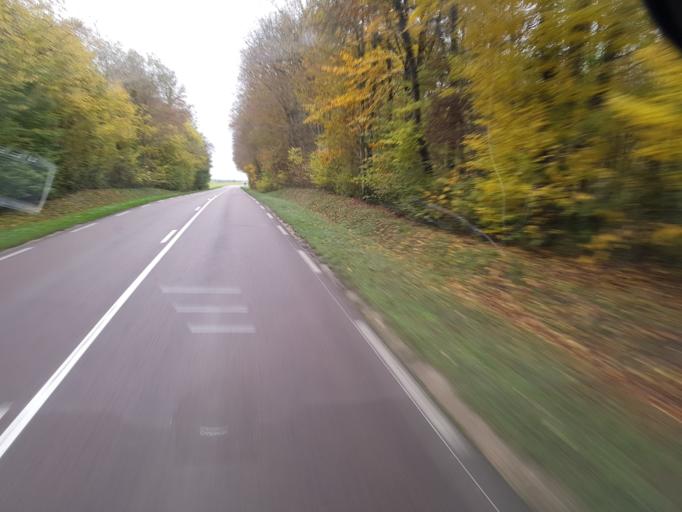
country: FR
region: Champagne-Ardenne
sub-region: Departement de la Marne
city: Esternay
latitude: 48.7960
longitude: 3.6201
